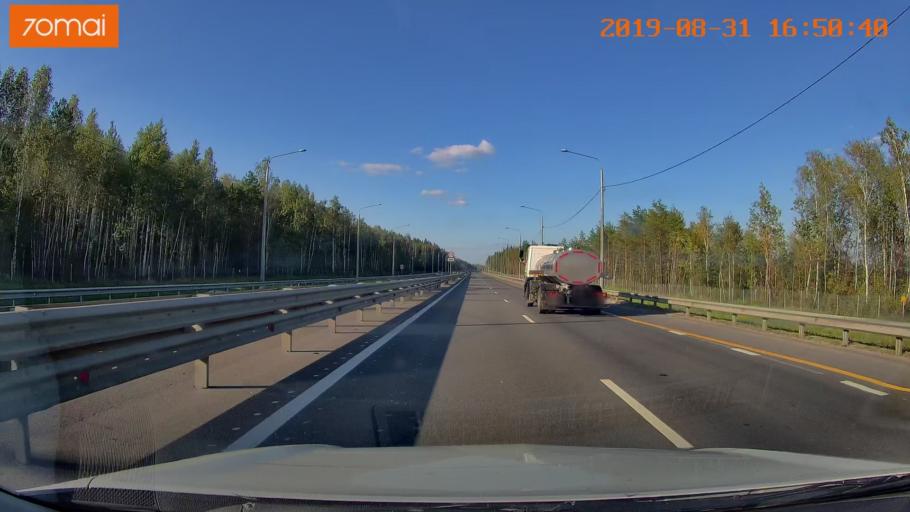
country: RU
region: Kaluga
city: Pyatovskiy
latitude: 54.7128
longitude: 36.1644
